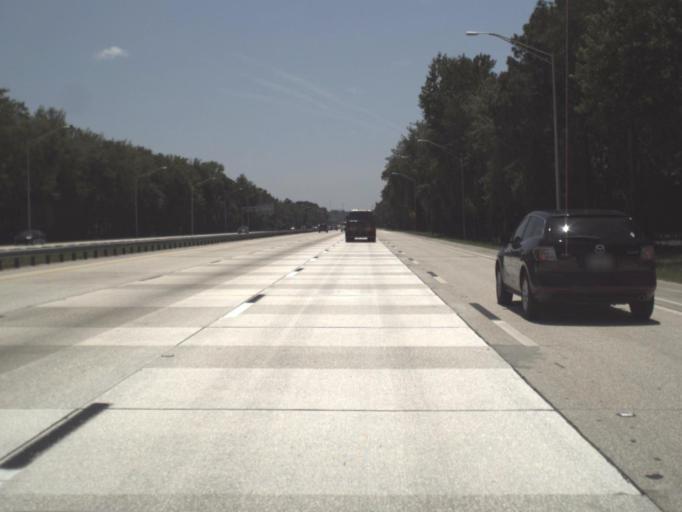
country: US
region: Florida
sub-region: Saint Johns County
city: Fruit Cove
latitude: 30.2150
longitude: -81.5676
